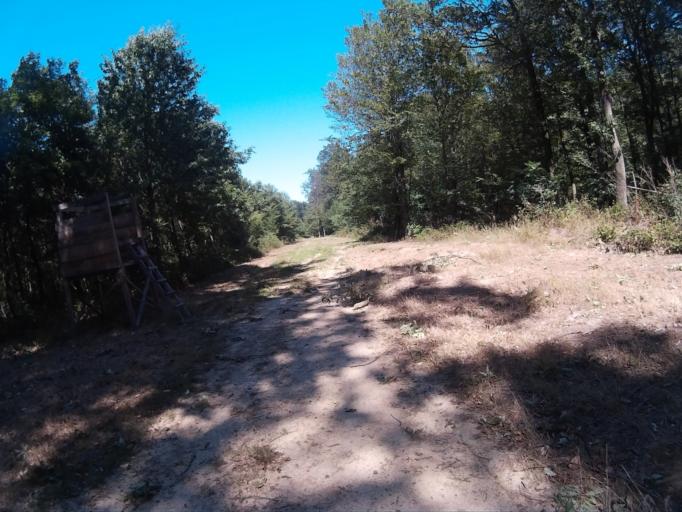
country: HU
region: Zala
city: Zalalovo
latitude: 46.8064
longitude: 16.6379
